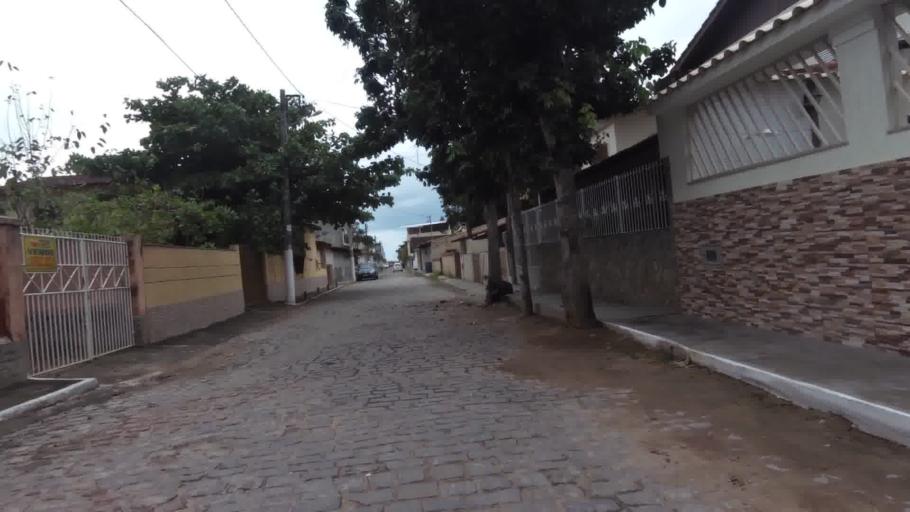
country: BR
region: Espirito Santo
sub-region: Marataizes
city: Marataizes
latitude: -21.0438
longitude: -40.8301
